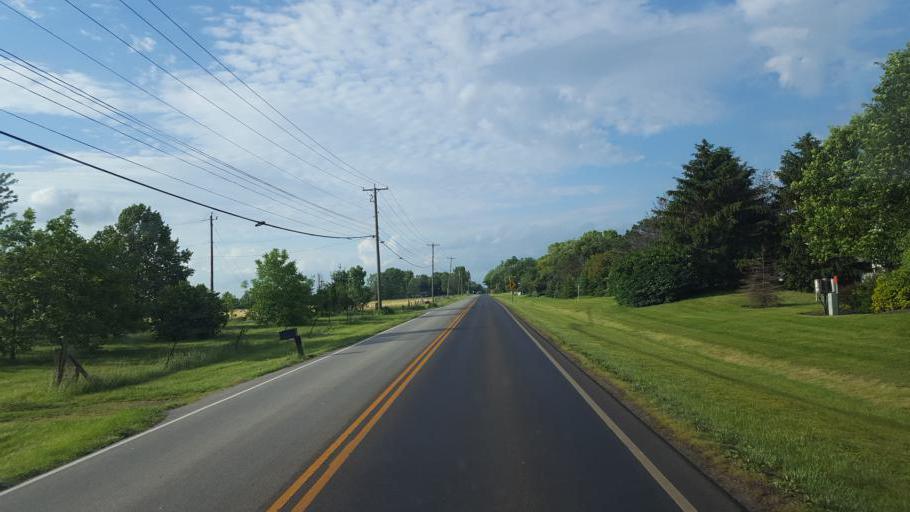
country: US
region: Ohio
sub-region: Delaware County
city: Lewis Center
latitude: 40.2125
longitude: -82.9857
